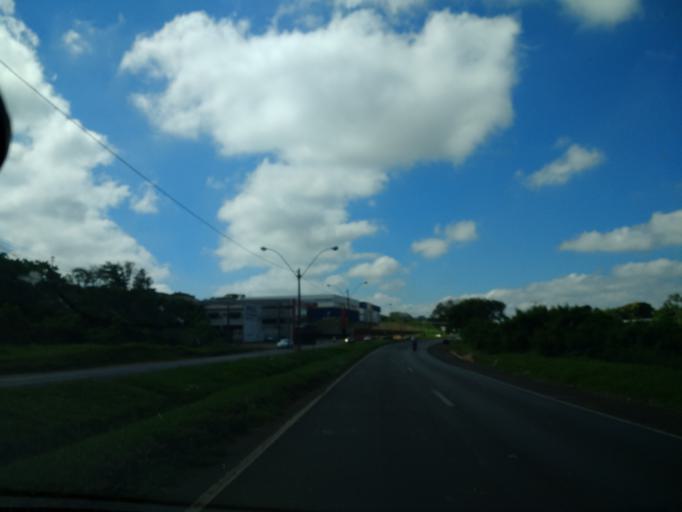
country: BR
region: Parana
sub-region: Umuarama
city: Umuarama
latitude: -23.7790
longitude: -53.3008
